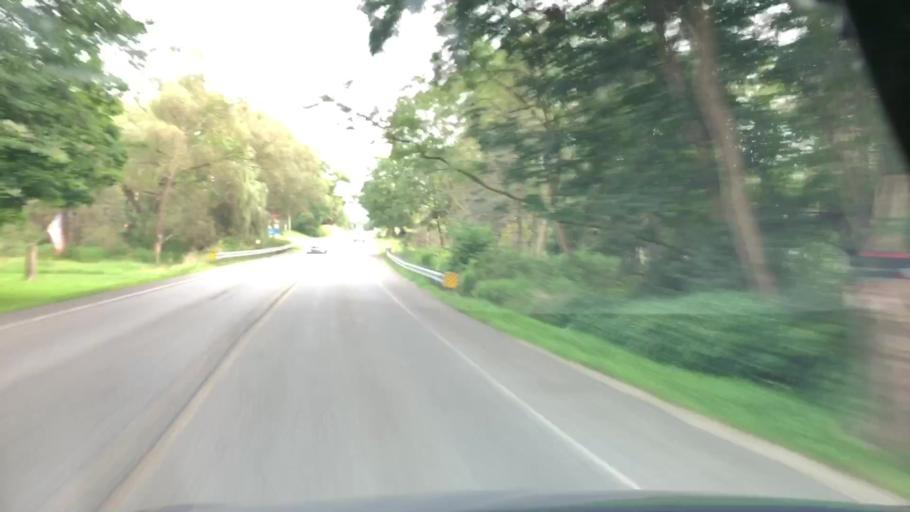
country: US
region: Pennsylvania
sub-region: Erie County
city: Union City
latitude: 41.8272
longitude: -79.8115
